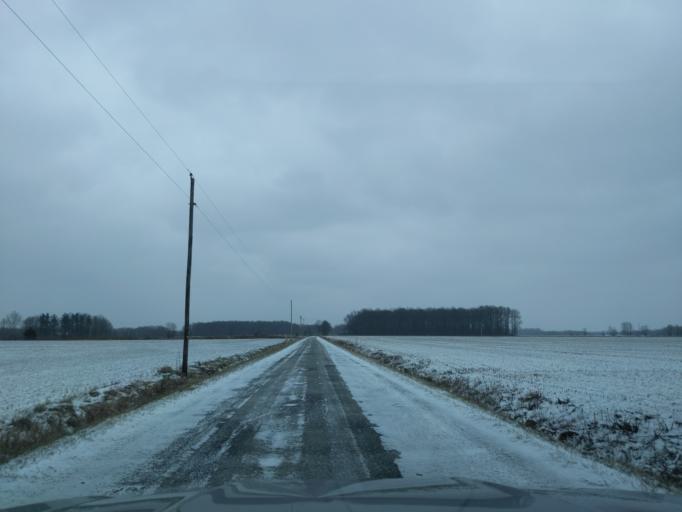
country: US
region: Indiana
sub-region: Decatur County
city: Westport
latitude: 39.2048
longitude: -85.4673
